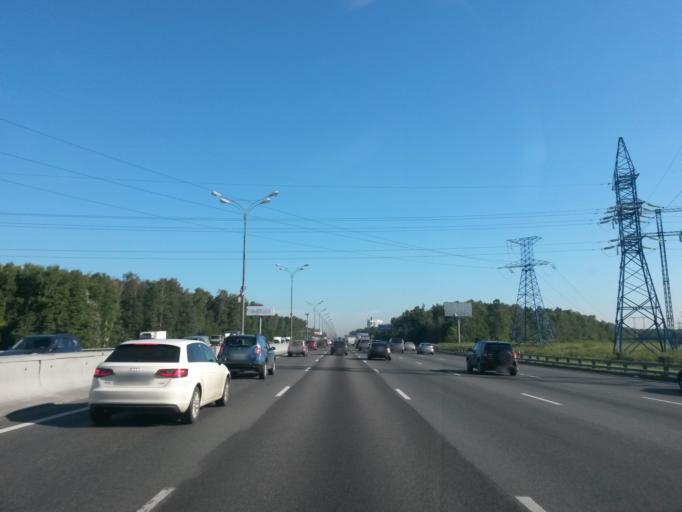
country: RU
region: Moscow
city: Ivanovskoye
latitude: 55.7874
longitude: 37.8417
